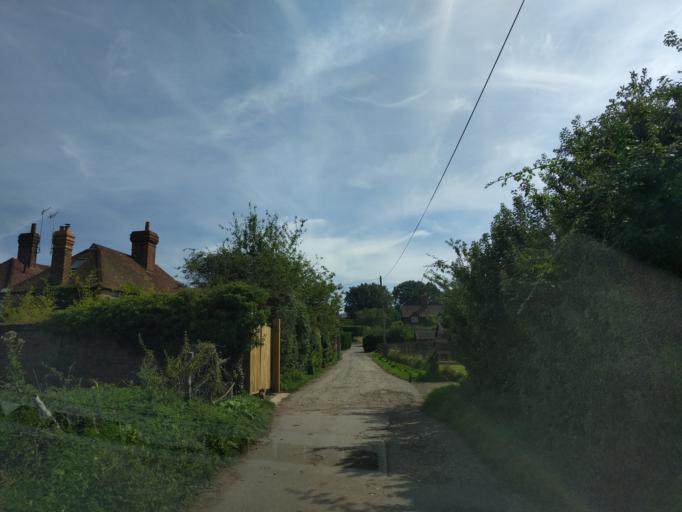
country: GB
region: England
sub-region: Surrey
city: Chilworth
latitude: 51.2173
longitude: -0.5195
